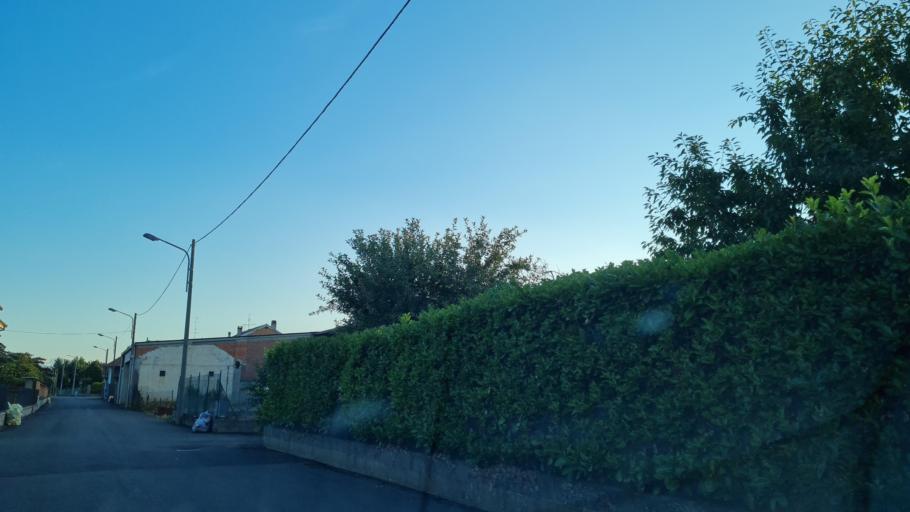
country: IT
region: Piedmont
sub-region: Provincia di Vercelli
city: Ghislarengo
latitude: 45.5273
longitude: 8.3850
